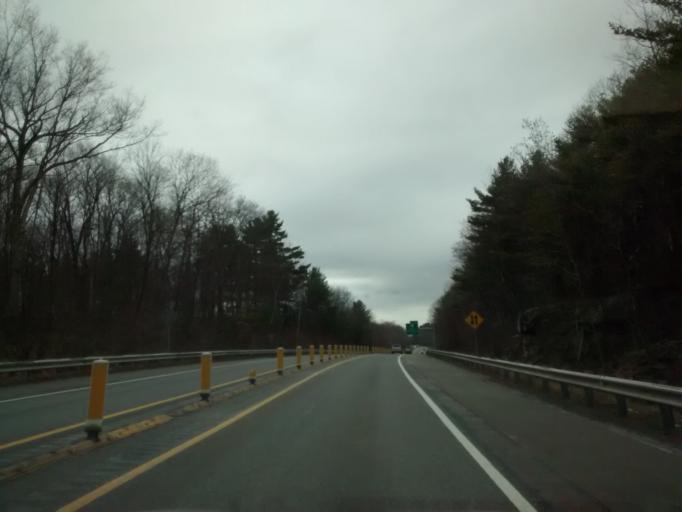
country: US
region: Massachusetts
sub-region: Worcester County
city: Phillipston
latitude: 42.5726
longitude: -72.1555
